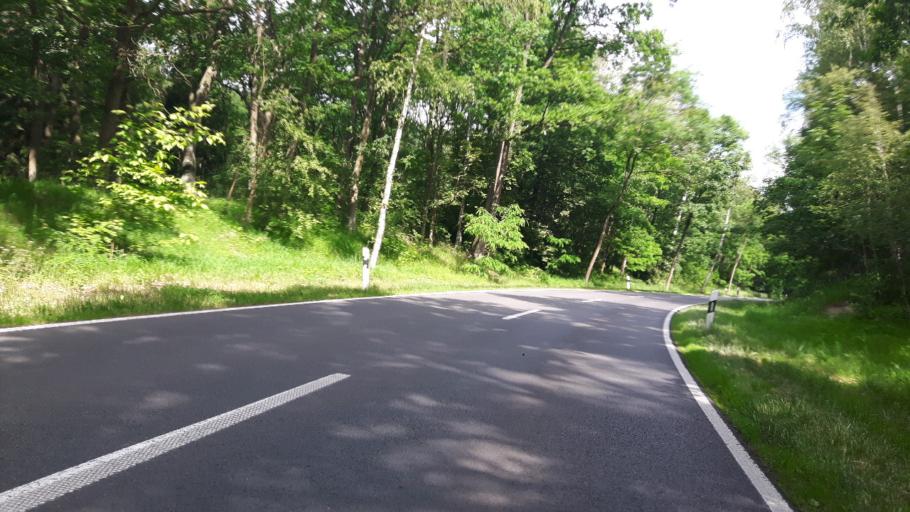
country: DE
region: Brandenburg
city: Mescherin
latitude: 53.2638
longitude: 14.4308
